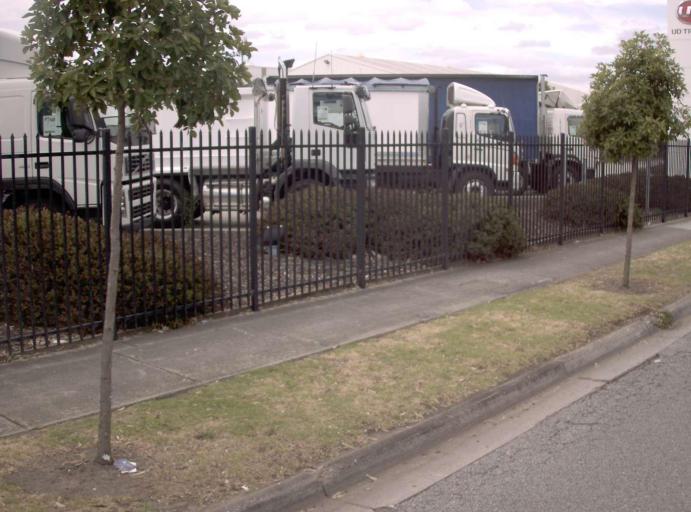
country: AU
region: Victoria
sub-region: Greater Dandenong
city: Springvale
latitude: -37.9323
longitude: 145.1496
